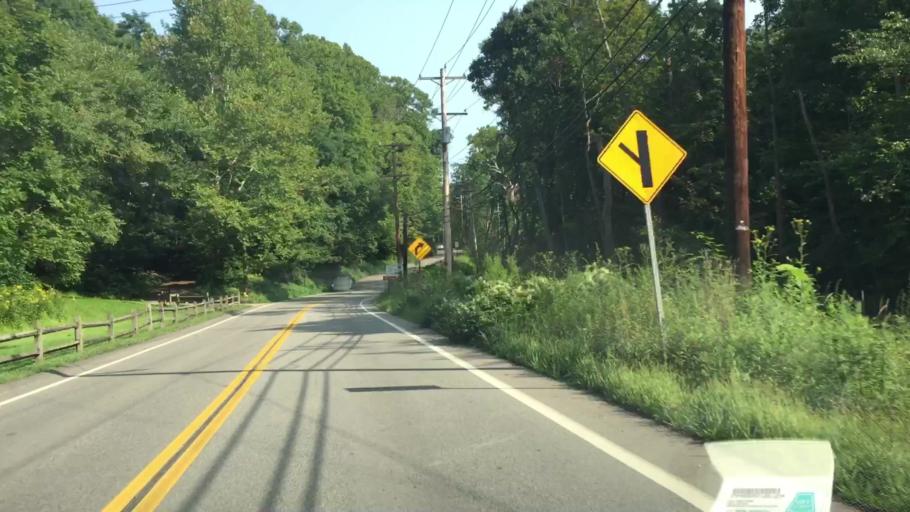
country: US
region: Pennsylvania
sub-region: Allegheny County
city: Fox Chapel
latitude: 40.5029
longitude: -79.8835
